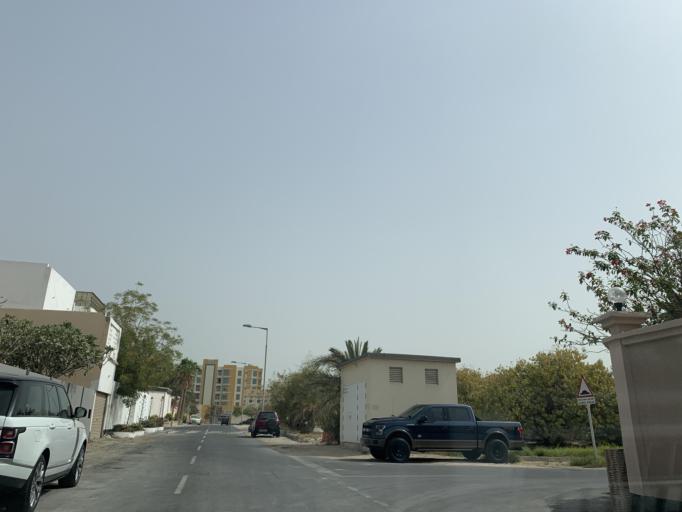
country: BH
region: Northern
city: Madinat `Isa
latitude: 26.1681
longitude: 50.5491
